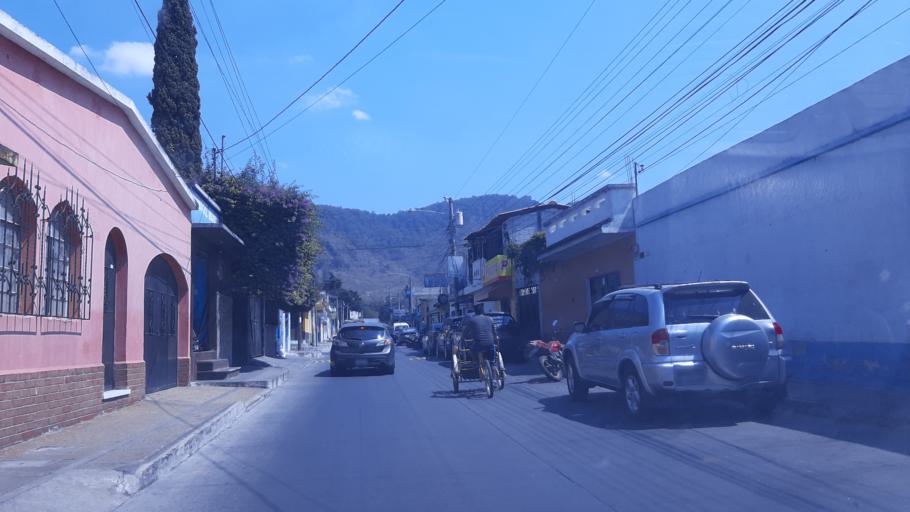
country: GT
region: Guatemala
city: Amatitlan
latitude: 14.4843
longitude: -90.6188
